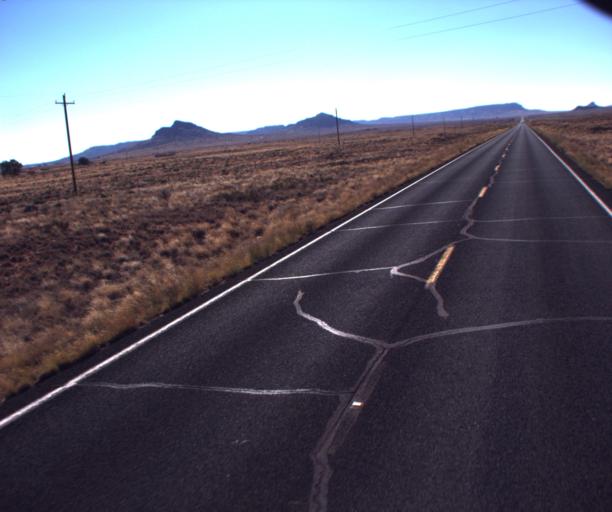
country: US
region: Arizona
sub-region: Navajo County
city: Dilkon
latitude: 35.5127
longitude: -110.4390
